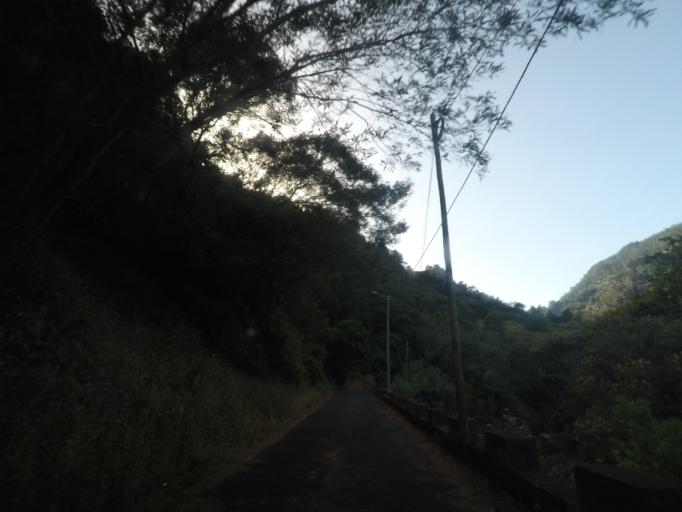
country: PT
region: Madeira
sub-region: Santa Cruz
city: Santa Cruz
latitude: 32.6933
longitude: -16.8052
